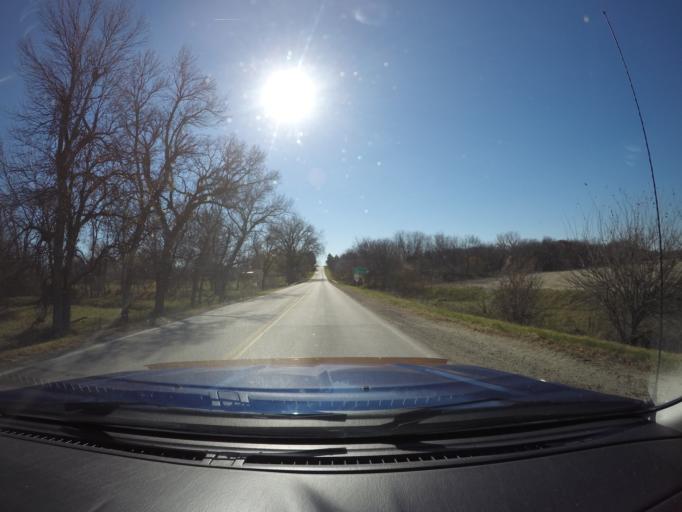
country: US
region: Kansas
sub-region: Marshall County
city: Marysville
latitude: 39.8592
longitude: -96.4170
